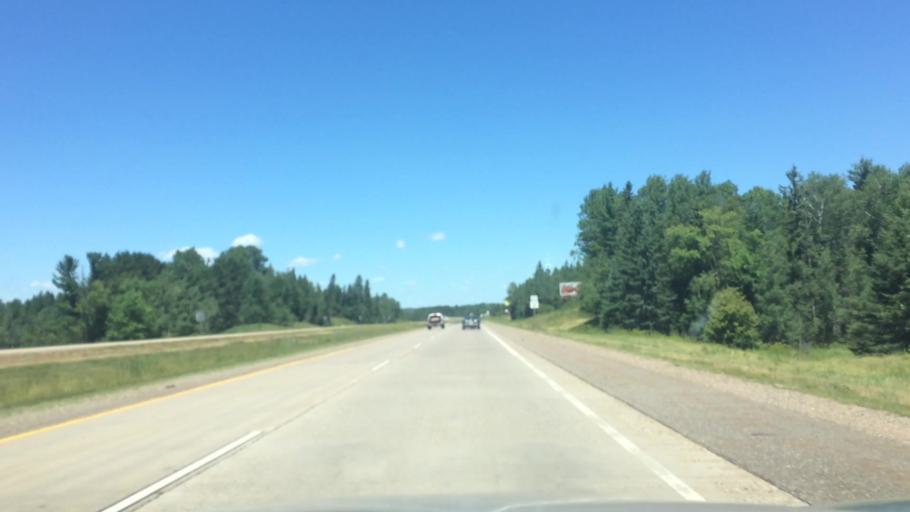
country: US
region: Wisconsin
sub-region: Lincoln County
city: Tomahawk
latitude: 45.3626
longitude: -89.6668
